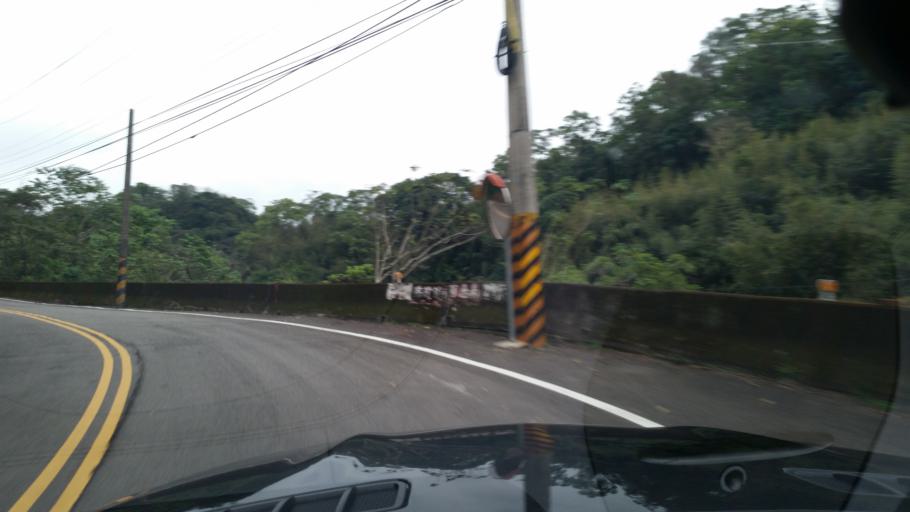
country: TW
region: Taiwan
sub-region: Miaoli
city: Miaoli
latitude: 24.5818
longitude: 120.8786
